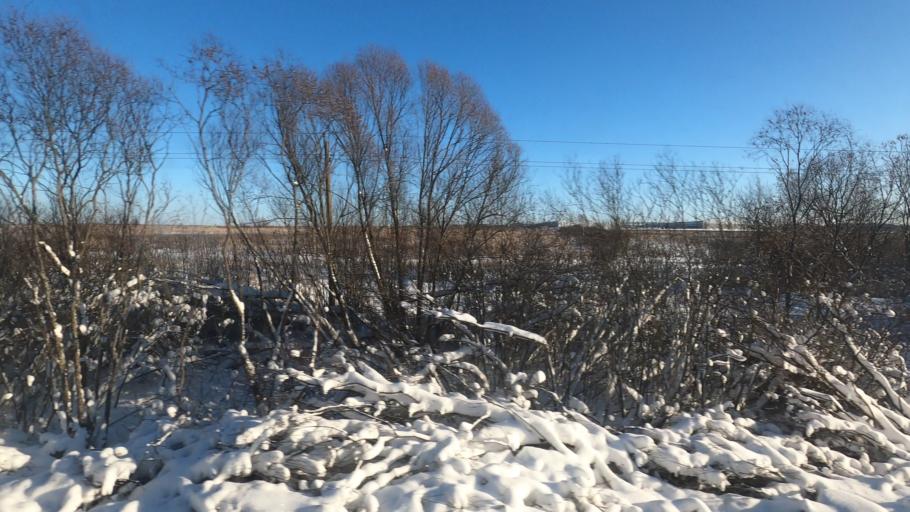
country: RU
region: Moskovskaya
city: Orud'yevo
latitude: 56.4231
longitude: 37.4979
